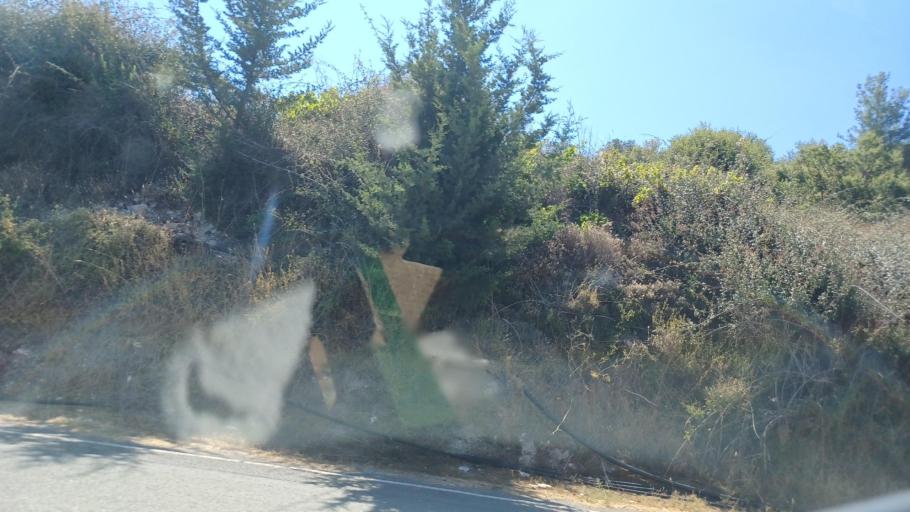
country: CY
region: Pafos
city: Mesogi
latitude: 34.9226
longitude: 32.6361
